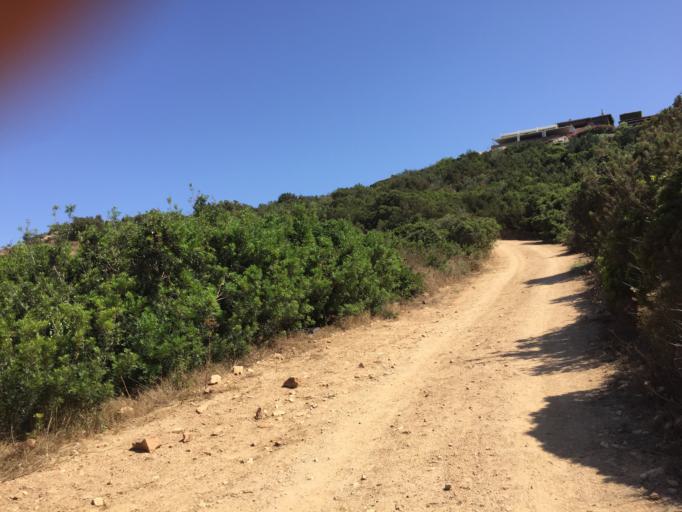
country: IT
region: Sardinia
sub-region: Provincia di Olbia-Tempio
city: San Teodoro
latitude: 40.8419
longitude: 9.7154
